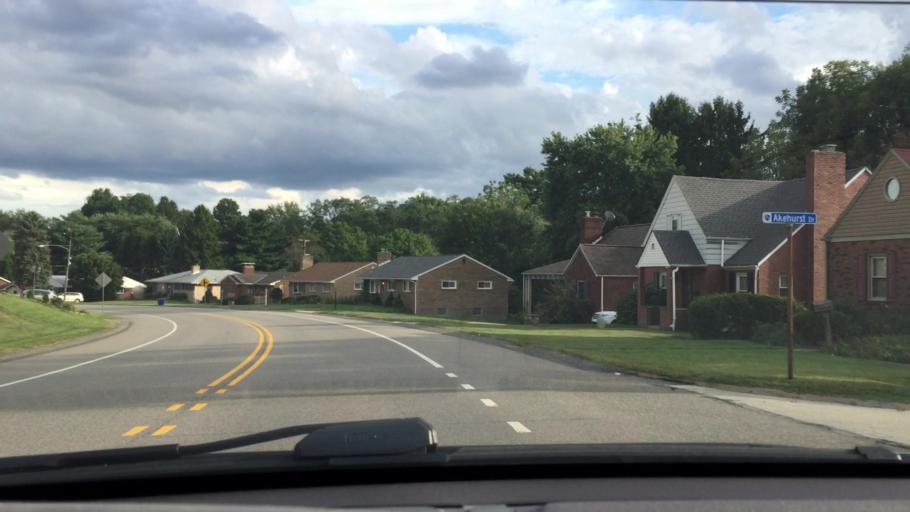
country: US
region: Pennsylvania
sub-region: Allegheny County
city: Green Tree
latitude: 40.4034
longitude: -80.0553
